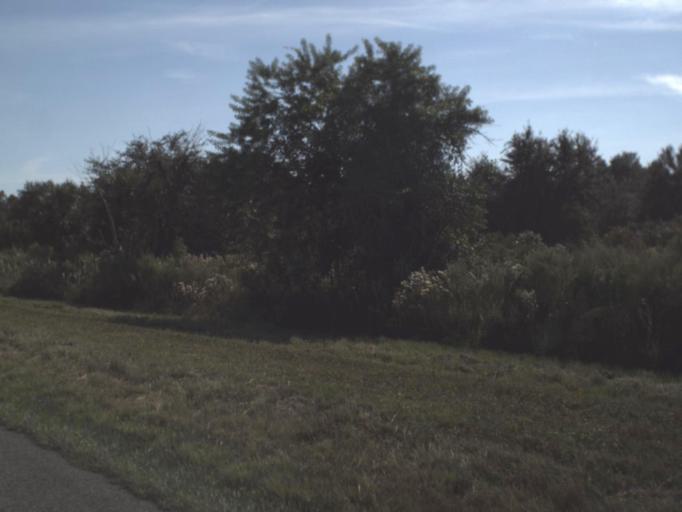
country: US
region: Florida
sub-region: Highlands County
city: Placid Lakes
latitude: 27.0088
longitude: -81.3335
